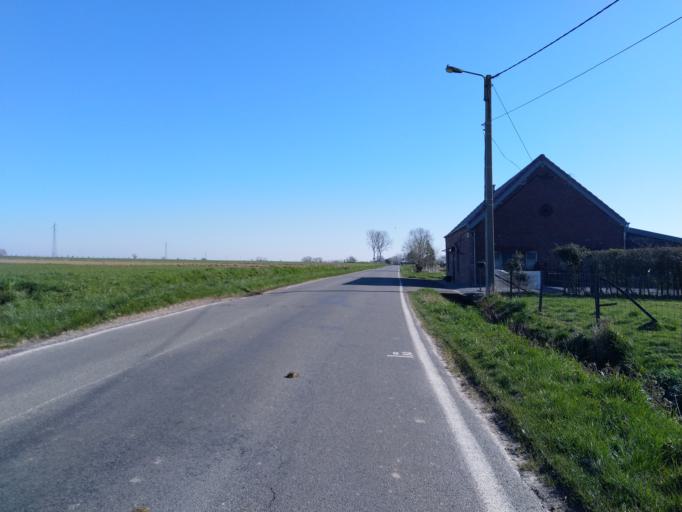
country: BE
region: Wallonia
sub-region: Province du Hainaut
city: Lens
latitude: 50.5472
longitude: 3.8645
